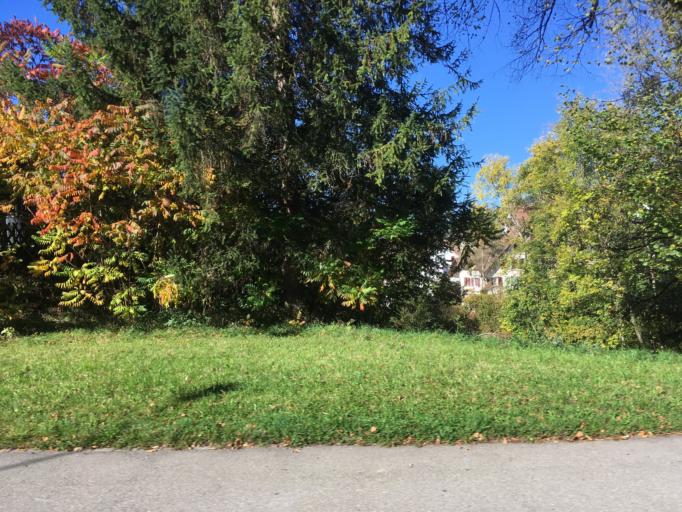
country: CH
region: Zurich
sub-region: Bezirk Hinwil
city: Baretswil
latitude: 47.3340
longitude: 8.8574
